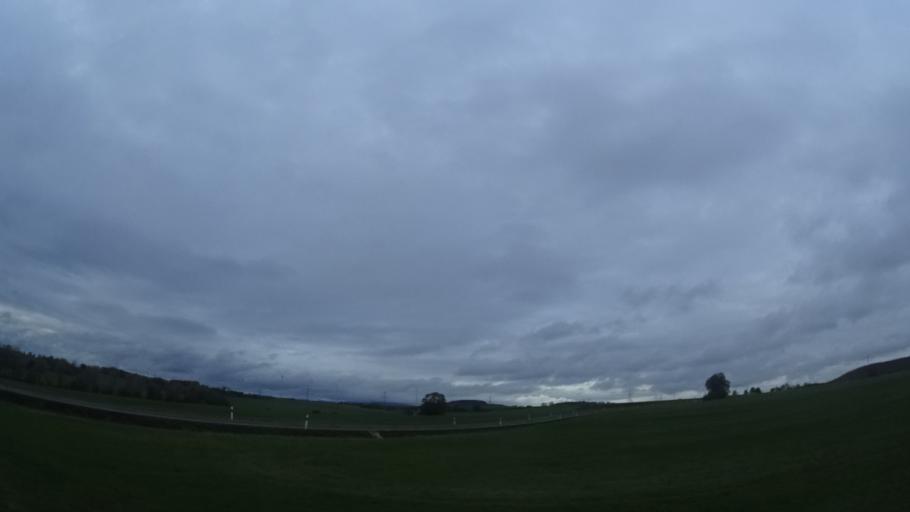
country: DE
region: Hesse
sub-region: Regierungsbezirk Giessen
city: Freiensteinau
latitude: 50.3797
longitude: 9.4298
